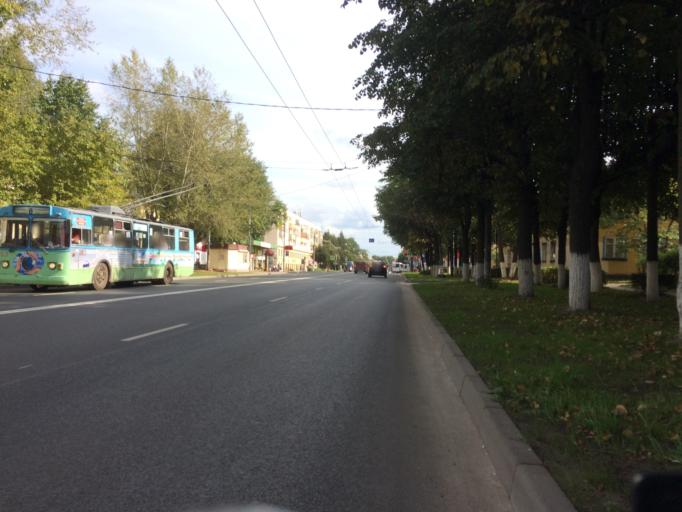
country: RU
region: Mariy-El
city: Yoshkar-Ola
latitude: 56.6377
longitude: 47.8723
